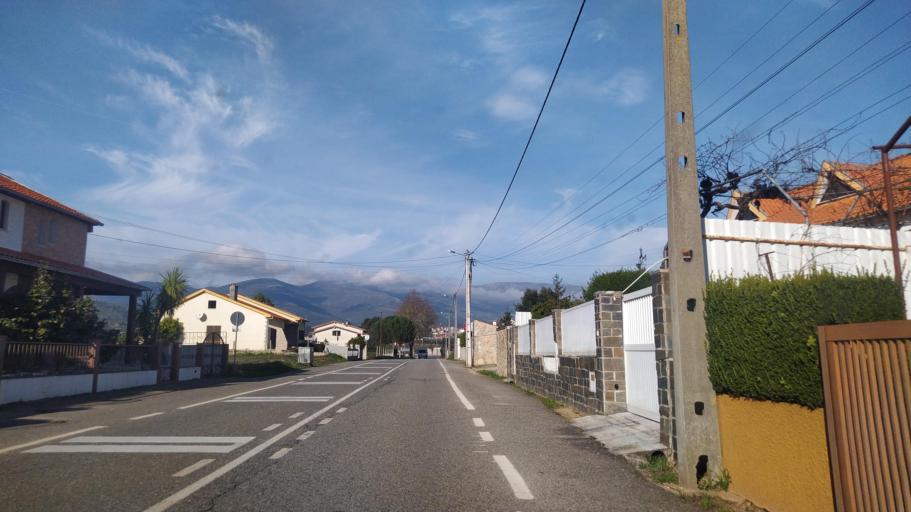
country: PT
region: Castelo Branco
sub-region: Concelho do Fundao
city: Aldeia de Joanes
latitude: 40.1889
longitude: -7.6376
